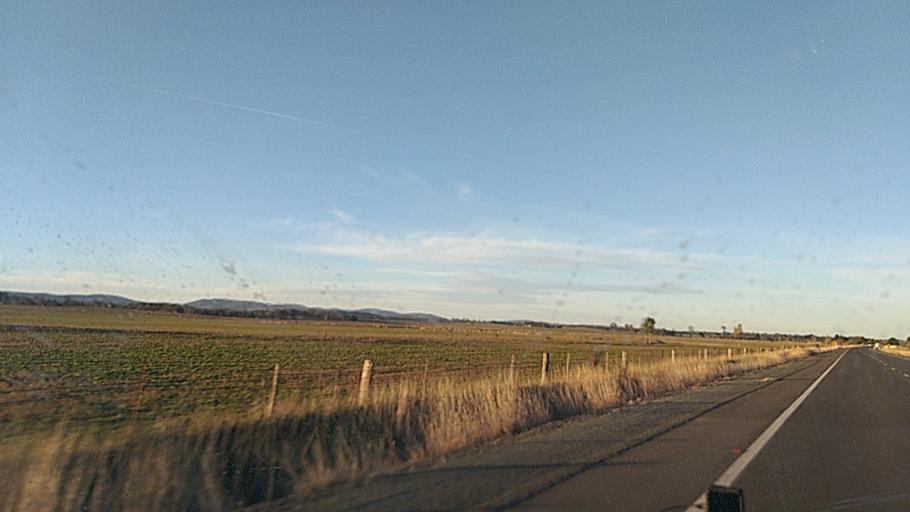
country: AU
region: New South Wales
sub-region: Goulburn Mulwaree
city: Goulburn
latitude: -34.8562
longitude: 149.5522
